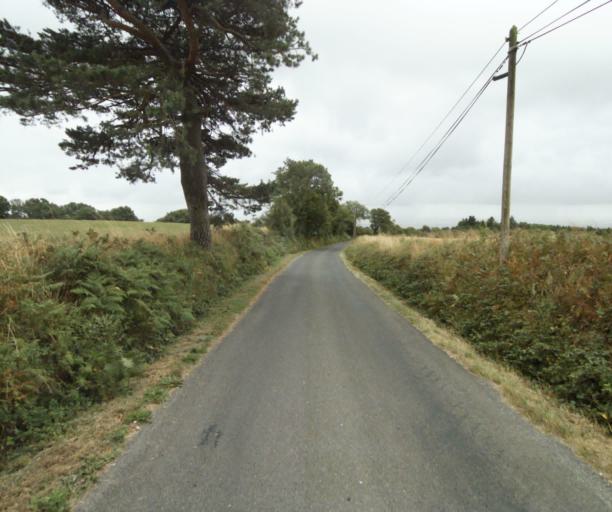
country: FR
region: Midi-Pyrenees
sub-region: Departement du Tarn
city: Soreze
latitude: 43.4031
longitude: 2.0640
